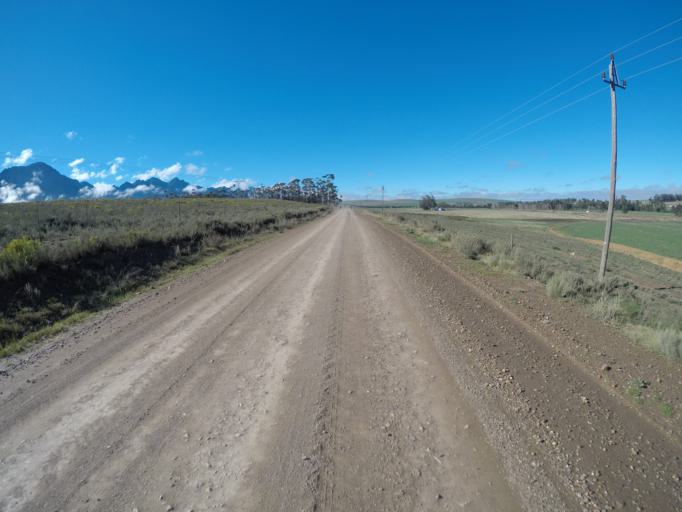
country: ZA
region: Western Cape
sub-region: Overberg District Municipality
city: Caledon
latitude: -34.0967
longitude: 19.6763
